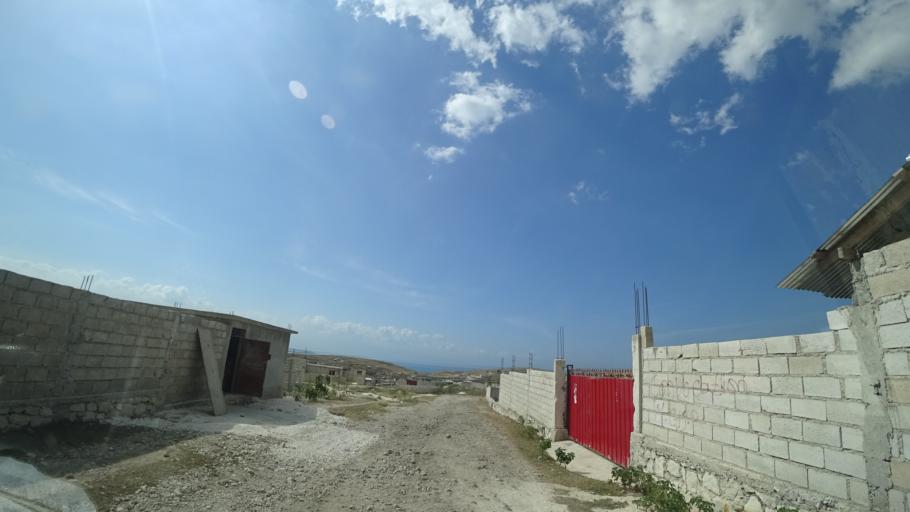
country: HT
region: Ouest
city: Cabaret
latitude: 18.6871
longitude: -72.3140
